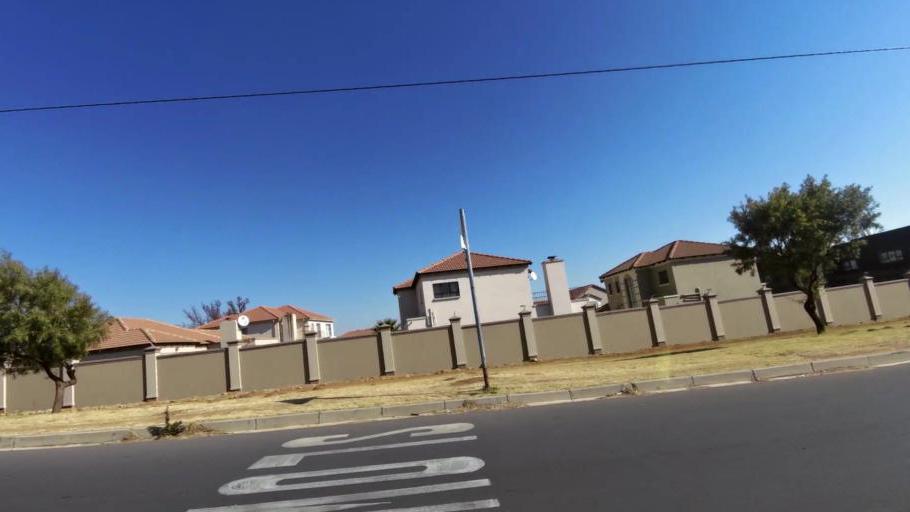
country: ZA
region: Gauteng
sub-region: City of Johannesburg Metropolitan Municipality
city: Johannesburg
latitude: -26.2407
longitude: 27.9987
